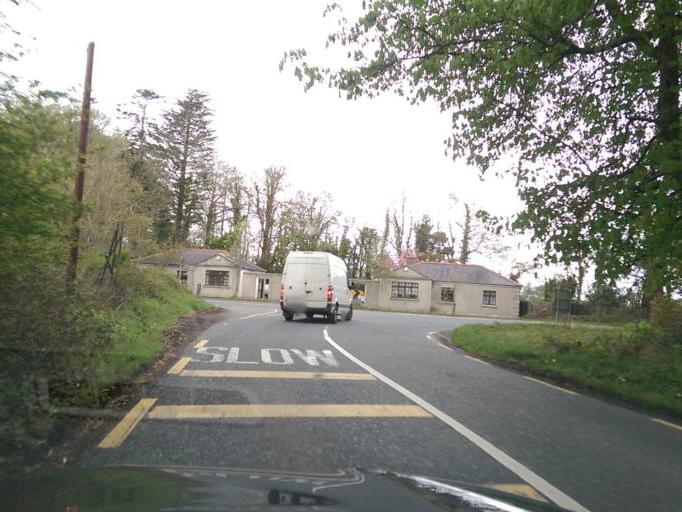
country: IE
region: Leinster
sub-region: An Mhi
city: Dunboyne
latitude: 53.3994
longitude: -6.4523
